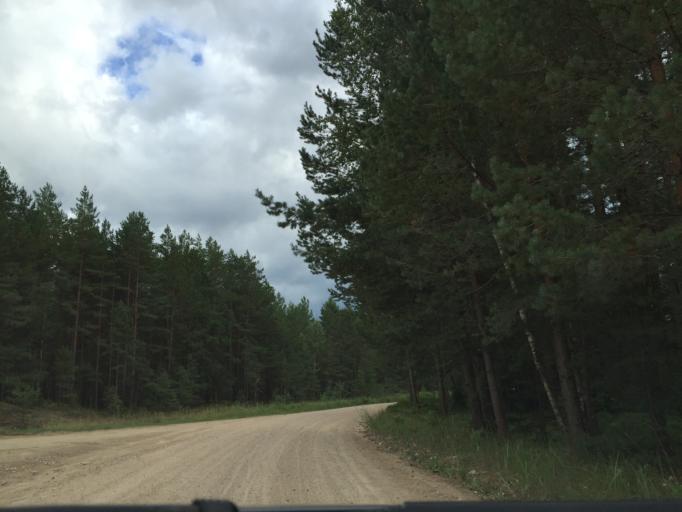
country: LV
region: Saulkrastu
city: Saulkrasti
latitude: 57.1762
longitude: 24.3813
